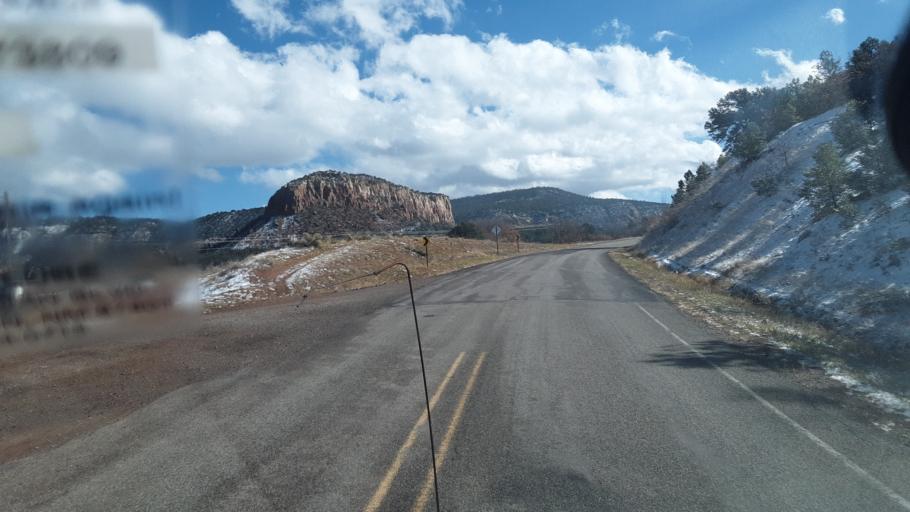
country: US
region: New Mexico
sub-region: Rio Arriba County
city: Santa Teresa
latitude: 36.2307
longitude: -106.8052
